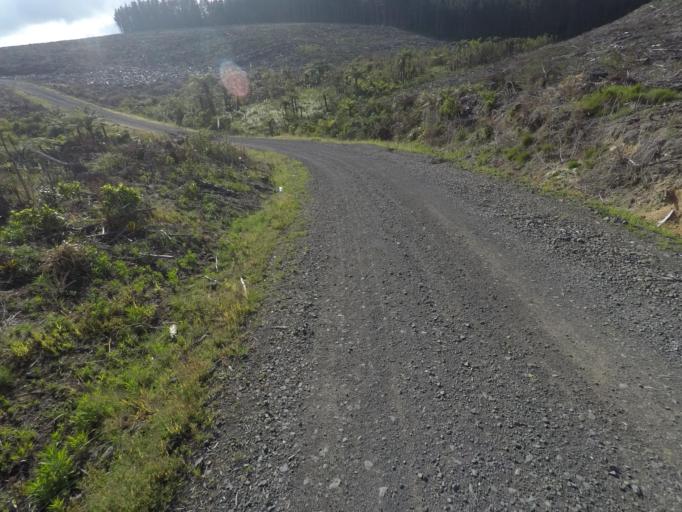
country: NZ
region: Auckland
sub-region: Auckland
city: Parakai
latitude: -36.7146
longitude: 174.5651
